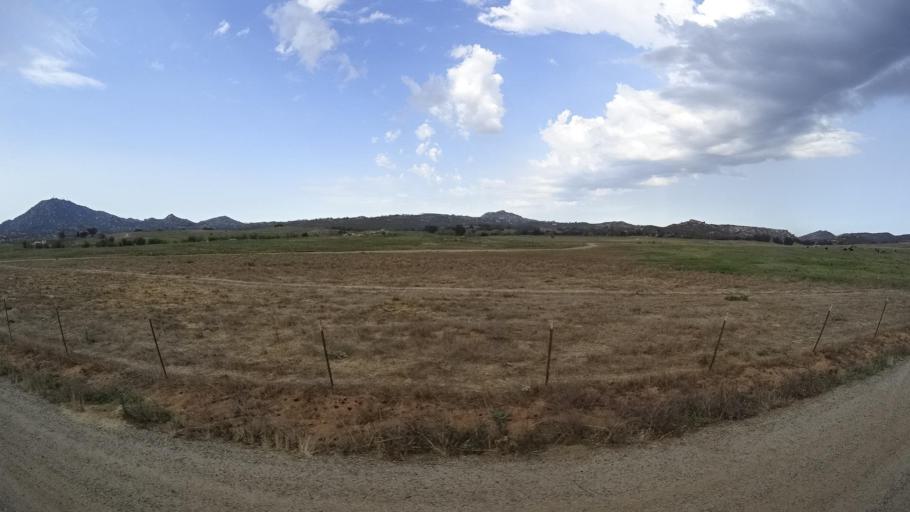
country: US
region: California
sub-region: San Diego County
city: San Pasqual
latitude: 33.0471
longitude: -116.9361
